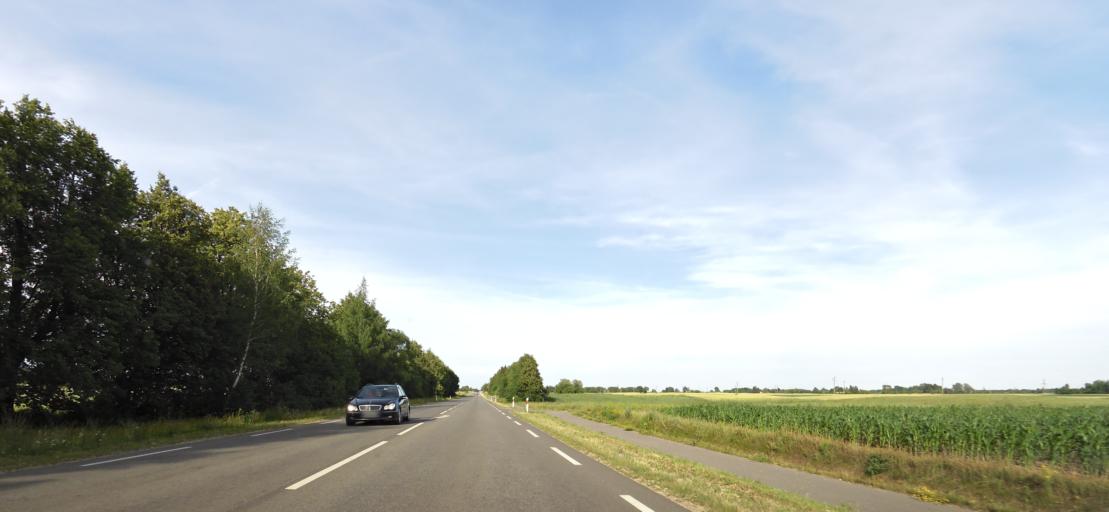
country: LT
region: Panevezys
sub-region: Birzai
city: Birzai
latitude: 56.1931
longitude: 24.6839
